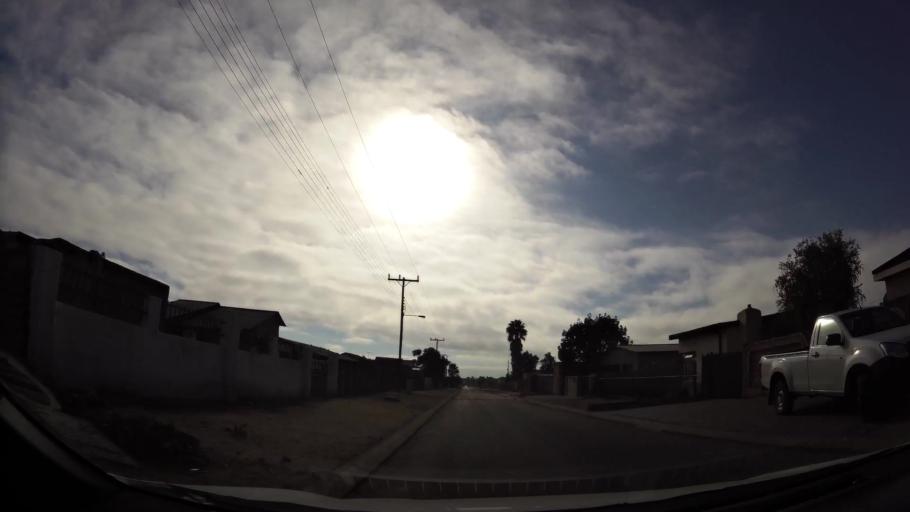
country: ZA
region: Limpopo
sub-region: Capricorn District Municipality
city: Polokwane
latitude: -23.8472
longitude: 29.3837
